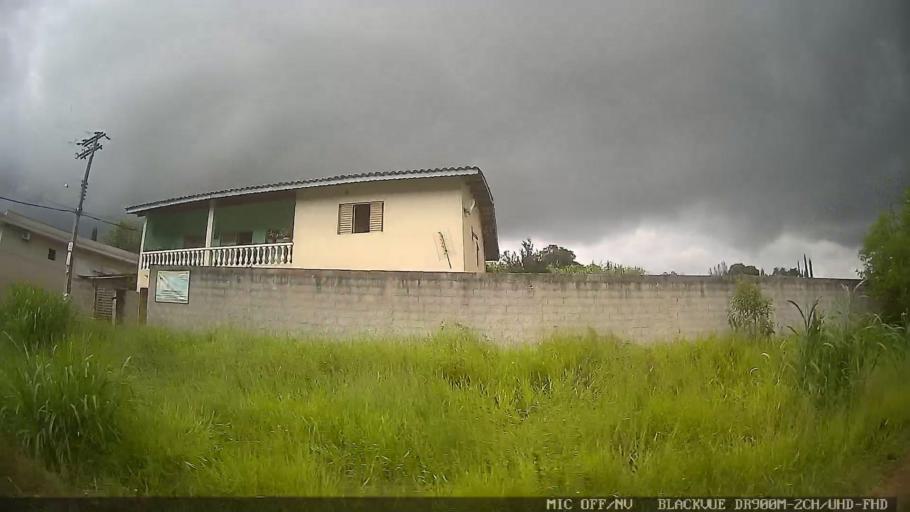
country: BR
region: Sao Paulo
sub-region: Atibaia
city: Atibaia
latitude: -23.1563
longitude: -46.5819
